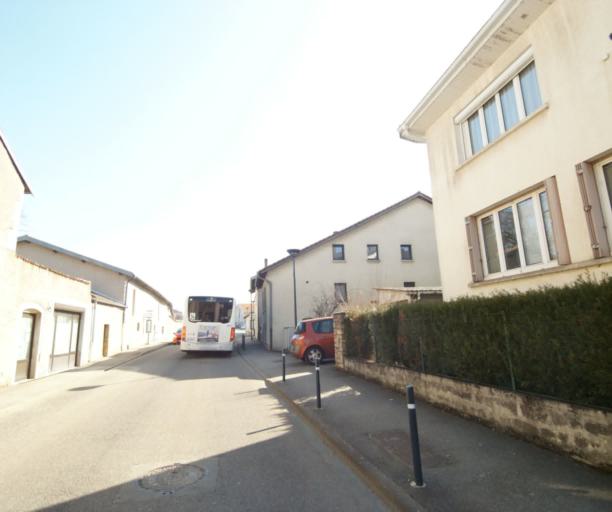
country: FR
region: Lorraine
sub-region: Departement de Meurthe-et-Moselle
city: Vandoeuvre-les-Nancy
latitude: 48.6455
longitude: 6.1749
